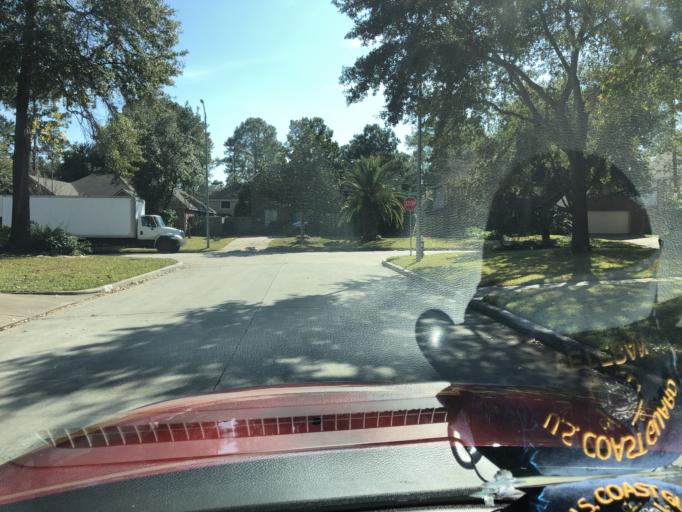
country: US
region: Texas
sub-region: Harris County
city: Tomball
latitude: 30.0216
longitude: -95.5531
